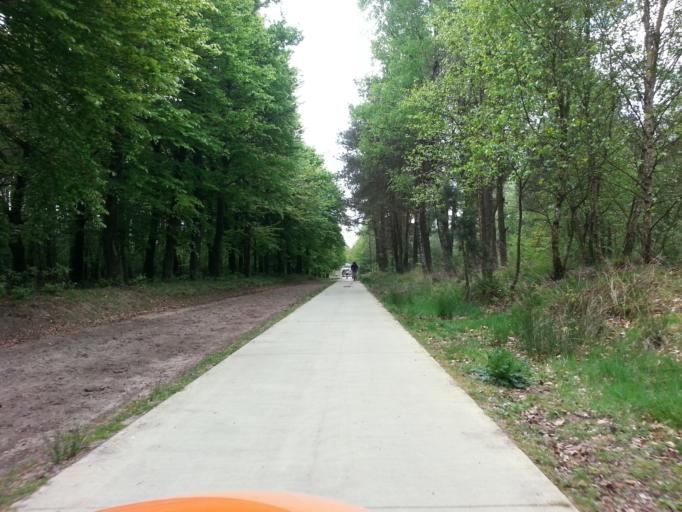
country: NL
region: Gelderland
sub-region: Gemeente Renkum
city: Heelsum
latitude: 52.0234
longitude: 5.7447
